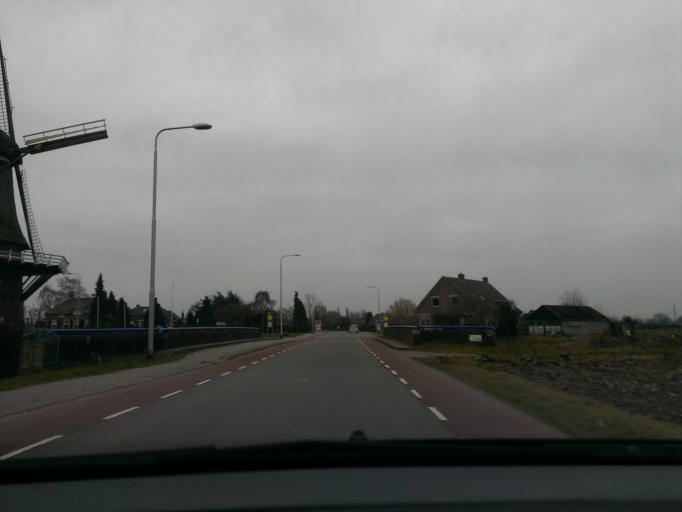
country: NL
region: Gelderland
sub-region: Gemeente Voorst
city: Twello
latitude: 52.2723
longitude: 6.1057
